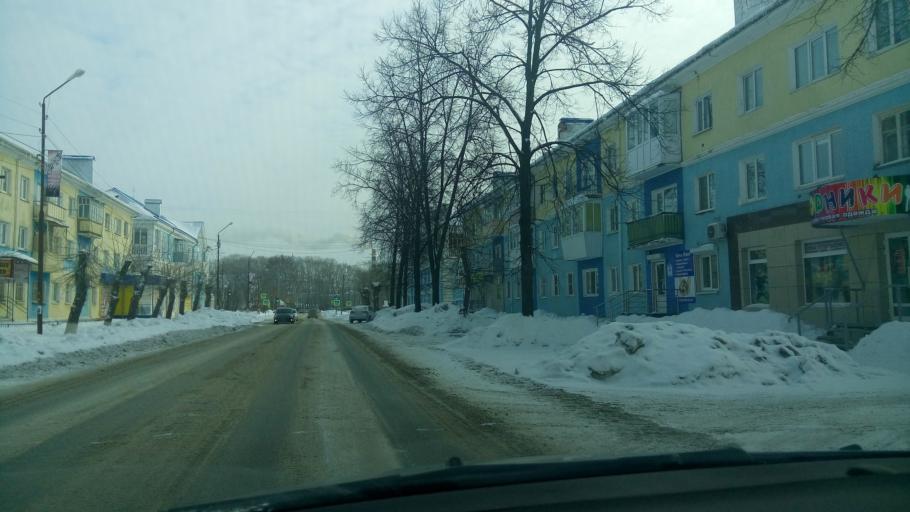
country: RU
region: Sverdlovsk
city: Bogdanovich
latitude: 56.7741
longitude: 62.0530
